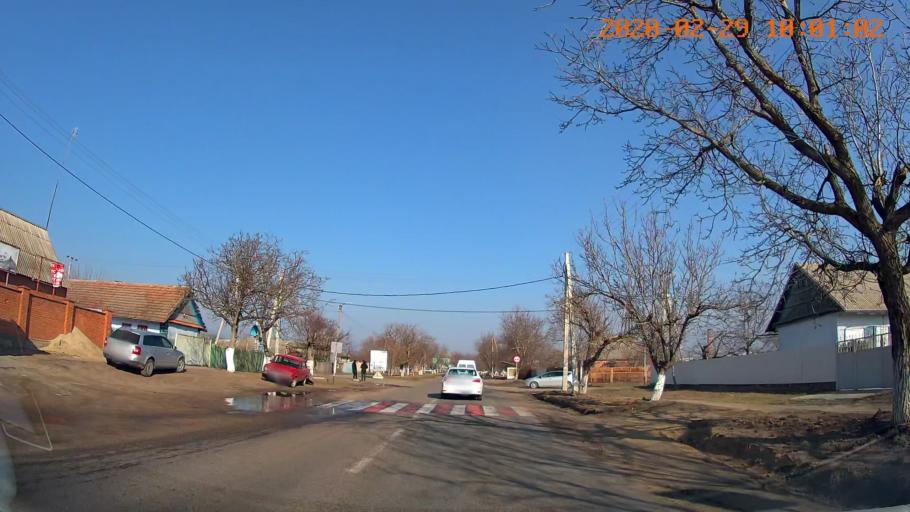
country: MD
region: Telenesti
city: Slobozia
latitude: 46.7726
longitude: 29.6854
